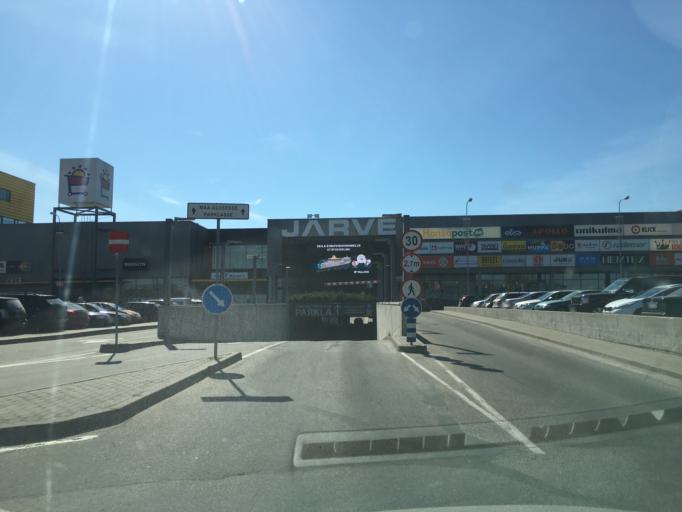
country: EE
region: Harju
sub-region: Tallinna linn
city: Tallinn
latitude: 59.3936
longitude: 24.7219
